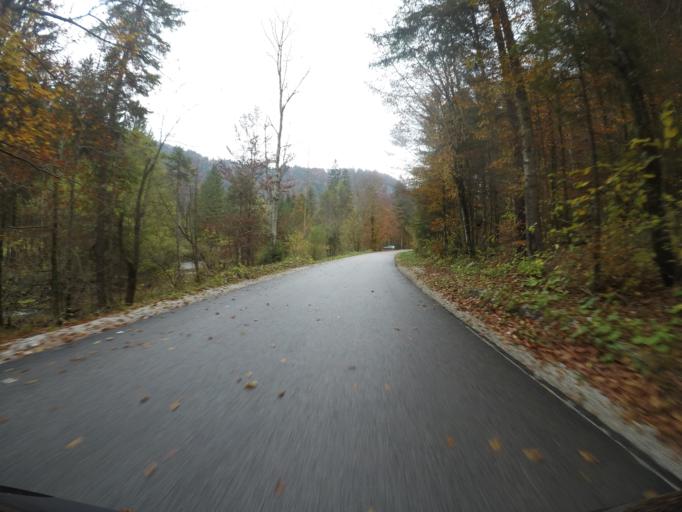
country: SI
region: Jesenice
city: Hrusica
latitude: 46.4172
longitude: 13.9890
